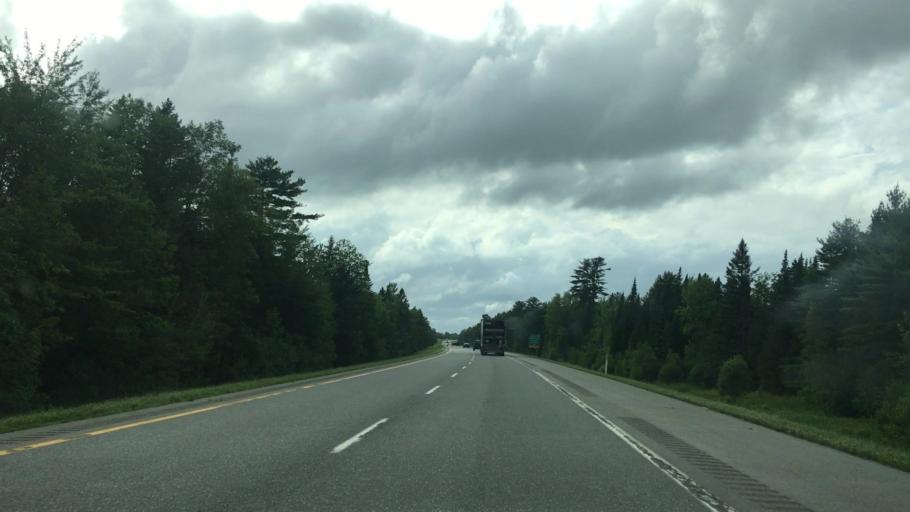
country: US
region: Maine
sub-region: Penobscot County
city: Newport
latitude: 44.8102
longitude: -69.2344
